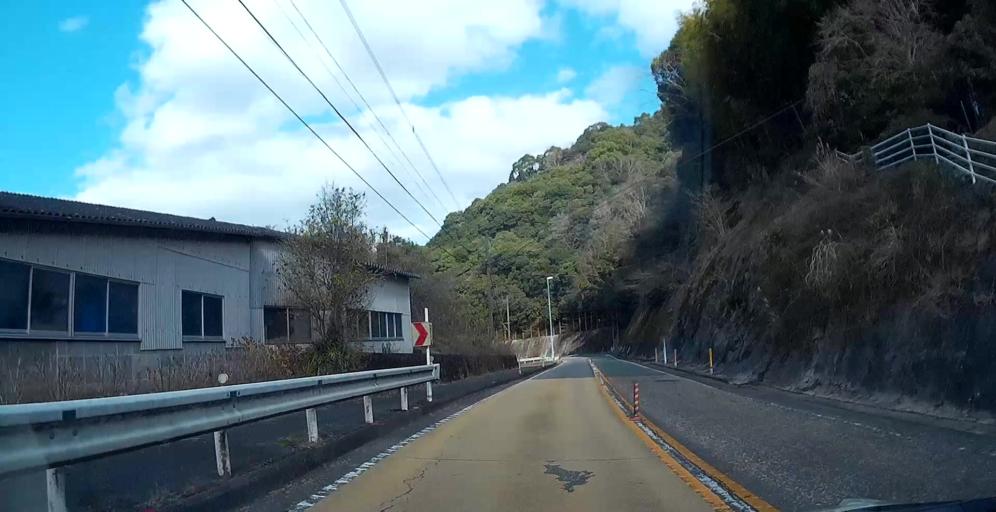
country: JP
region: Kumamoto
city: Yatsushiro
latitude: 32.3899
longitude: 130.5442
